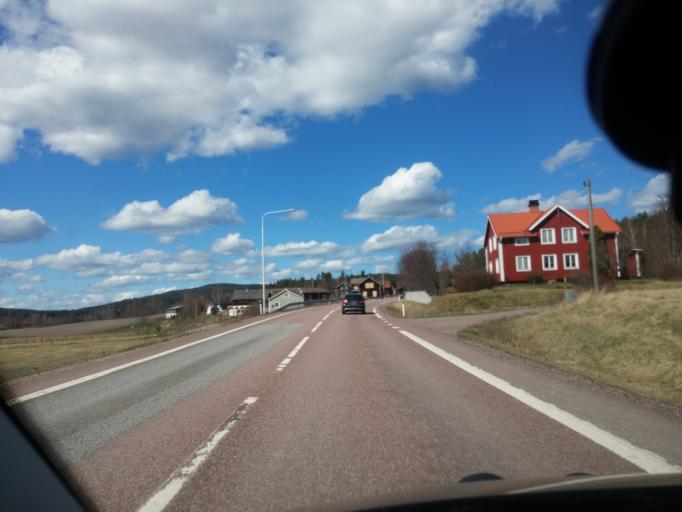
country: SE
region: Dalarna
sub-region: Faluns Kommun
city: Svardsjo
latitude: 60.7219
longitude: 15.7738
